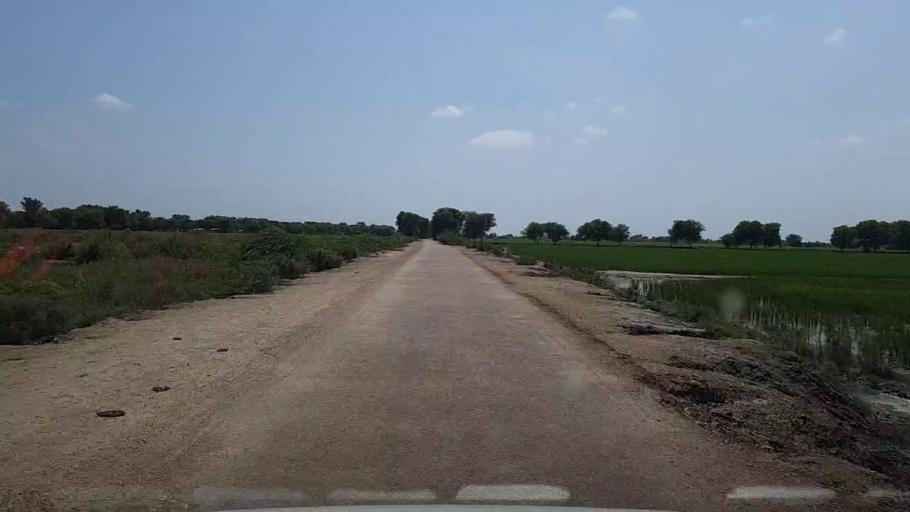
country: PK
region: Sindh
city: Kario
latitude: 24.8286
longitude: 68.7029
